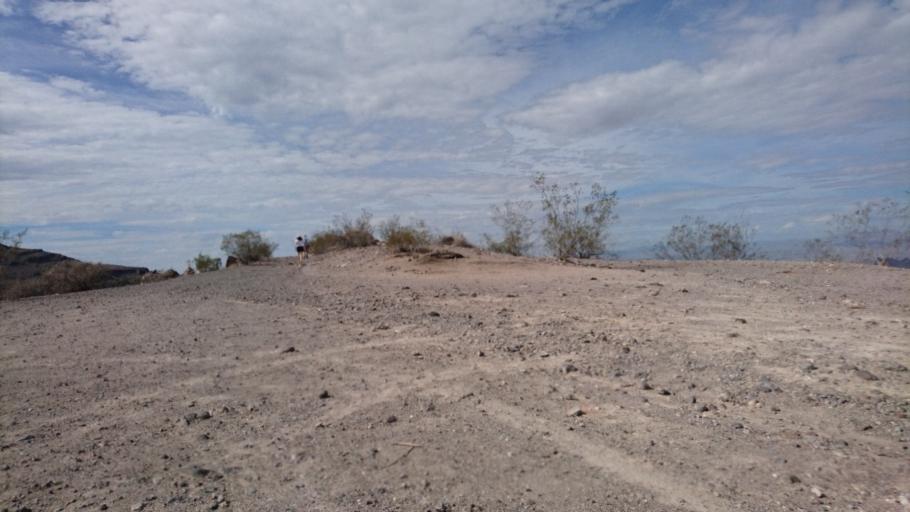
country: US
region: Arizona
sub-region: Mohave County
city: Golden Valley
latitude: 35.0470
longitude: -114.3636
